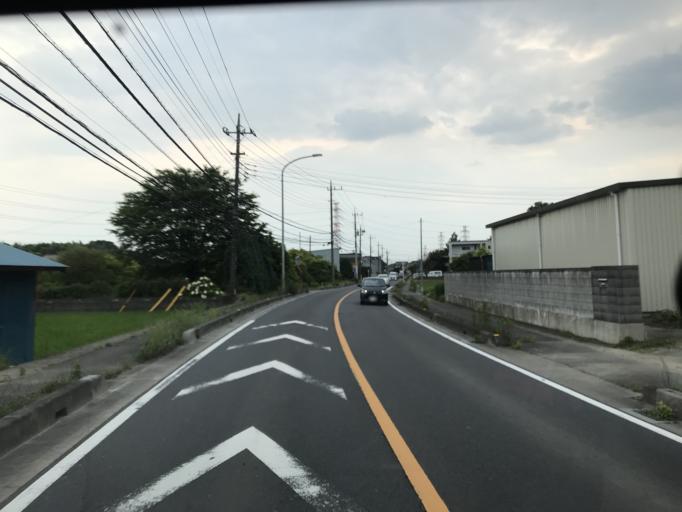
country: JP
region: Saitama
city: Shiraoka
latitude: 36.0103
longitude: 139.6913
